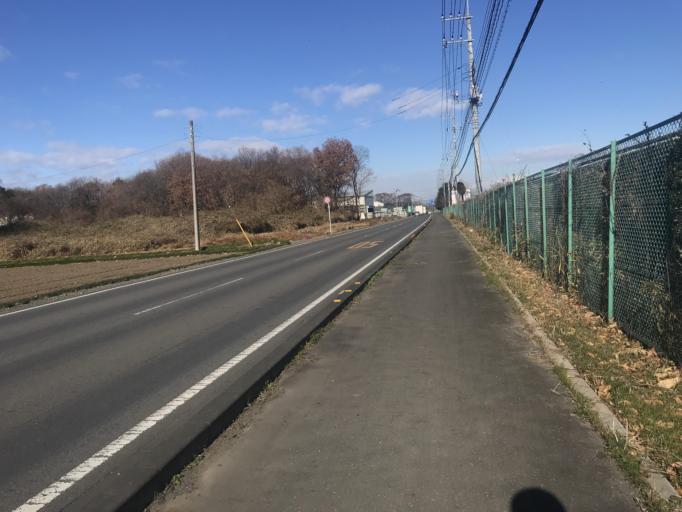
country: JP
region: Ibaraki
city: Yuki
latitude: 36.3468
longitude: 139.8785
